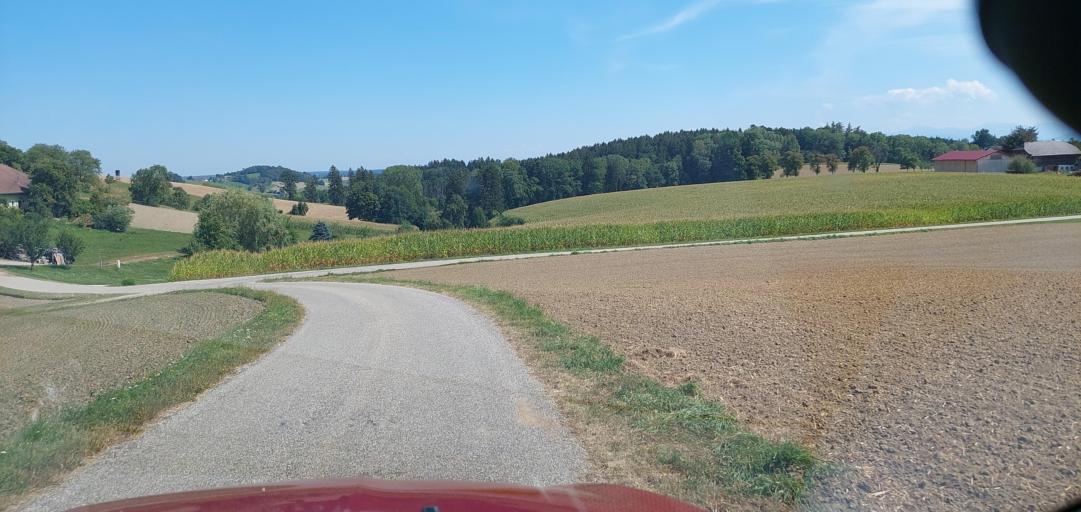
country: AT
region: Upper Austria
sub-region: Wels-Land
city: Pennewang
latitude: 48.1411
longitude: 13.8468
